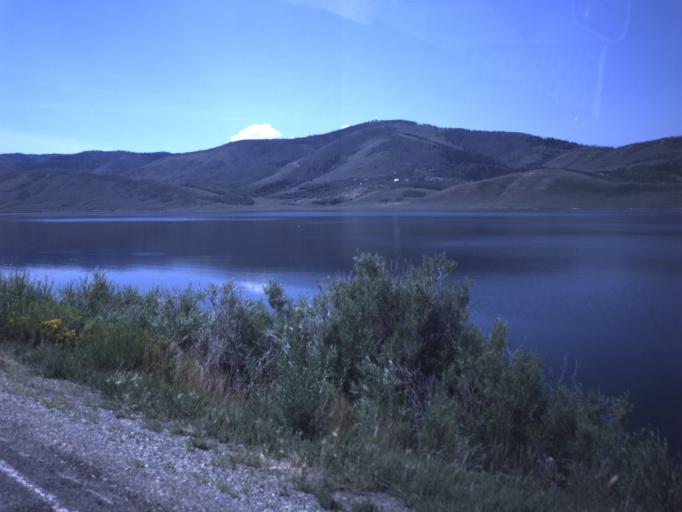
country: US
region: Utah
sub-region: Carbon County
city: Helper
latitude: 39.7727
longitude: -111.1391
